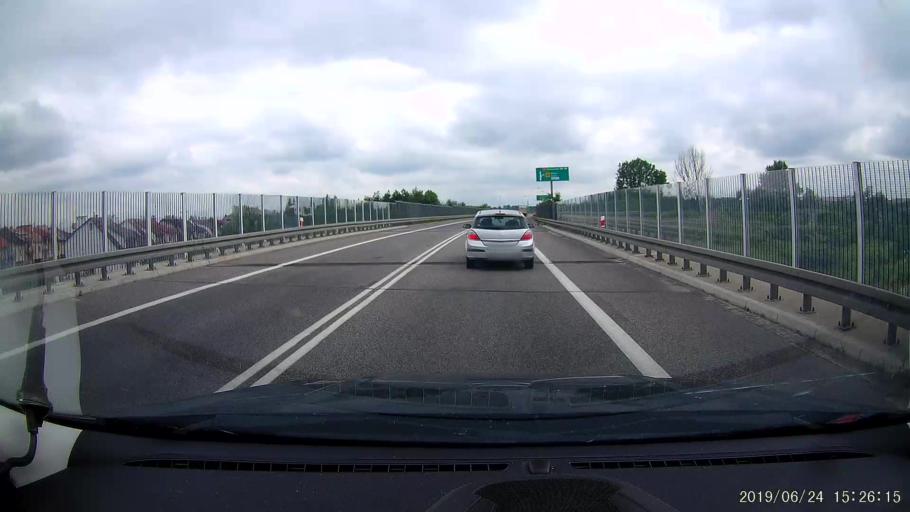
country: PL
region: Subcarpathian Voivodeship
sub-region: Powiat jaroslawski
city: Jaroslaw
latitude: 50.0261
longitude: 22.6923
